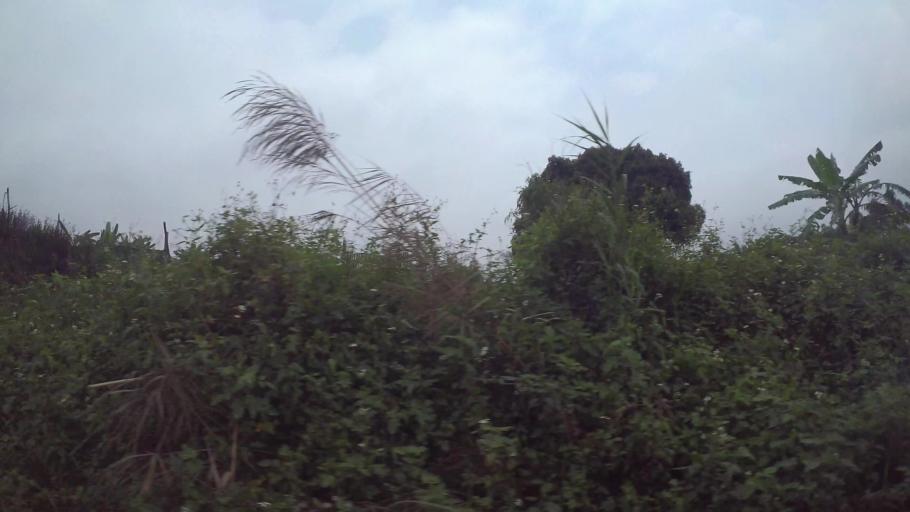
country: VN
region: Ha Noi
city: Van Dien
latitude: 20.9758
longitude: 105.8597
